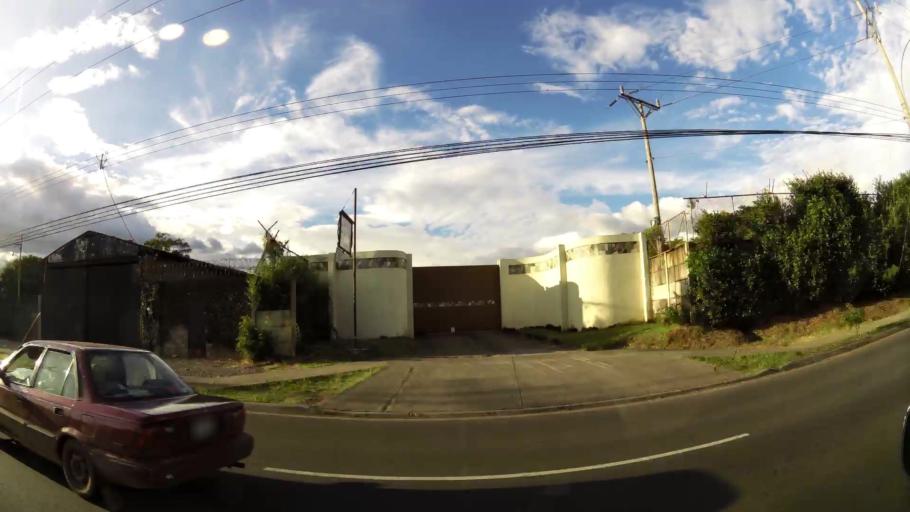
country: CR
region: Heredia
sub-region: Canton de Belen
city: San Antonio
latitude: 10.0066
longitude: -84.1784
